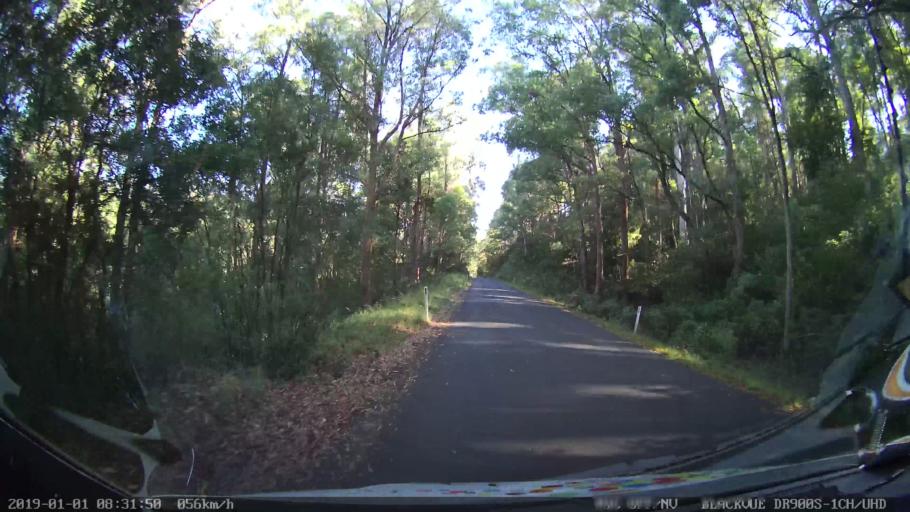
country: AU
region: New South Wales
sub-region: Snowy River
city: Jindabyne
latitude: -36.3671
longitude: 148.2055
